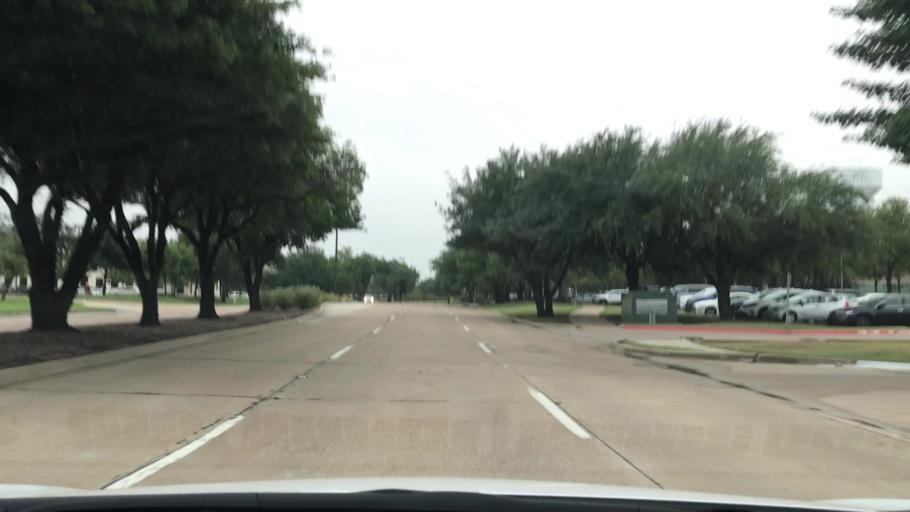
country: US
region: Texas
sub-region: Dallas County
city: Coppell
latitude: 32.9292
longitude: -97.0065
